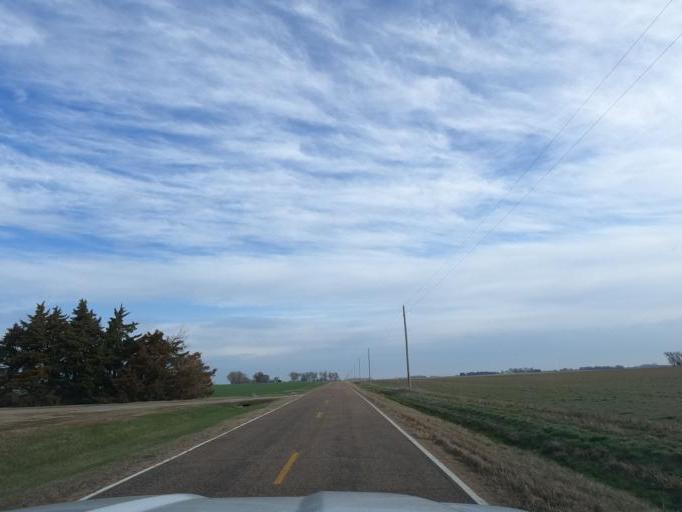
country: US
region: Kansas
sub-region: Rice County
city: Sterling
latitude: 38.0872
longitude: -98.2521
